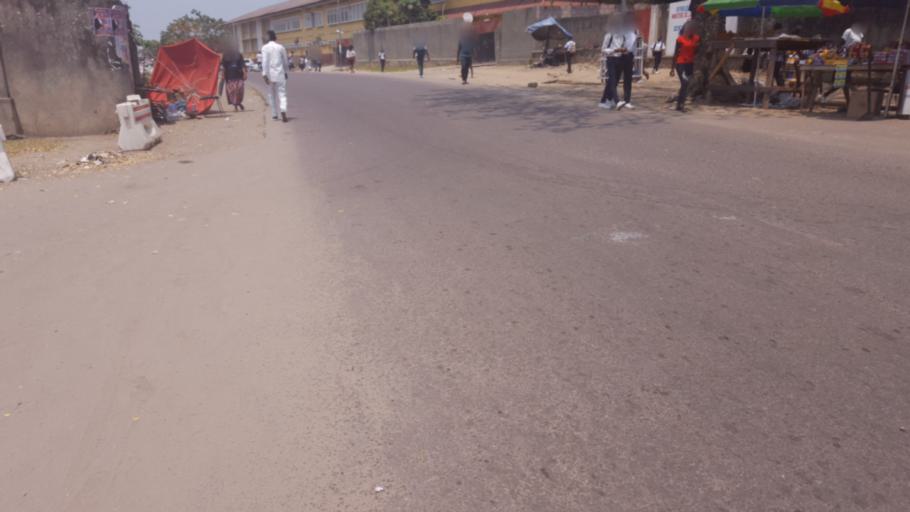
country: CD
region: Kinshasa
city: Kinshasa
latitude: -4.3224
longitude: 15.2924
